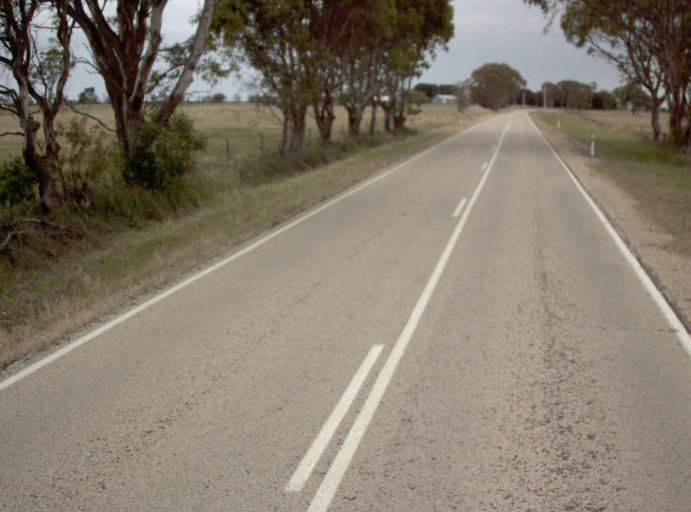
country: AU
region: Victoria
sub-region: East Gippsland
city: Bairnsdale
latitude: -37.9288
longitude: 147.5400
